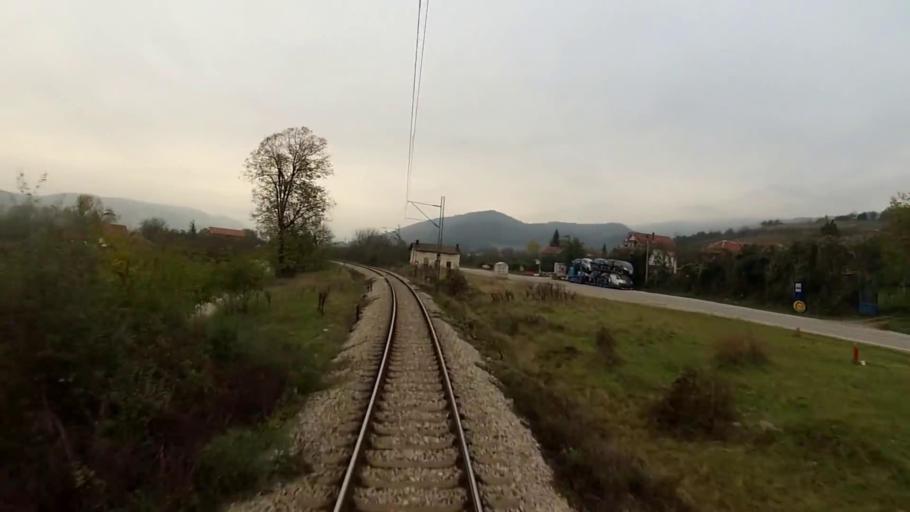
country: RS
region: Central Serbia
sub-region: Pirotski Okrug
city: Dimitrovgrad
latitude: 43.0049
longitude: 22.8087
